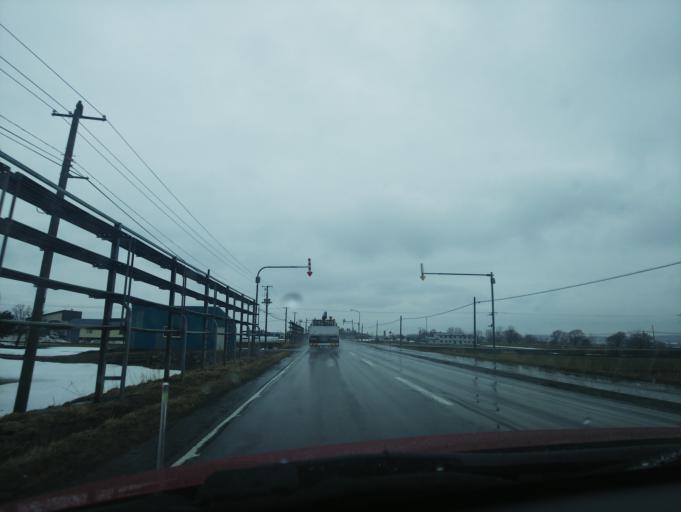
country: JP
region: Hokkaido
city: Nayoro
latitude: 44.2047
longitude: 142.3949
